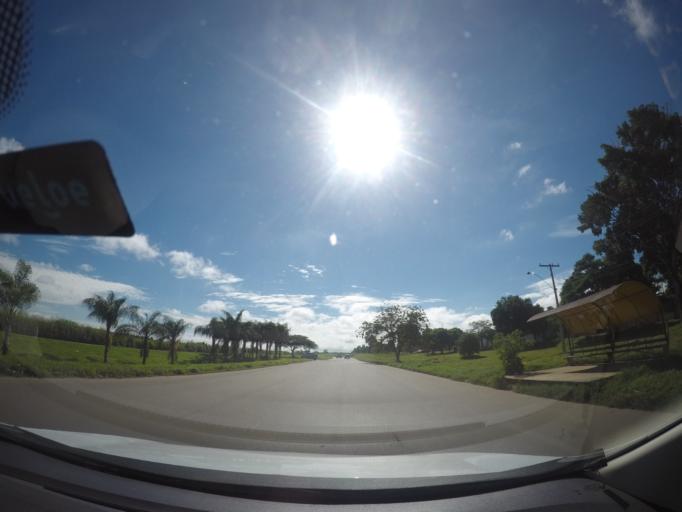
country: BR
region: Goias
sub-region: Senador Canedo
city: Senador Canedo
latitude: -16.6493
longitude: -49.1566
